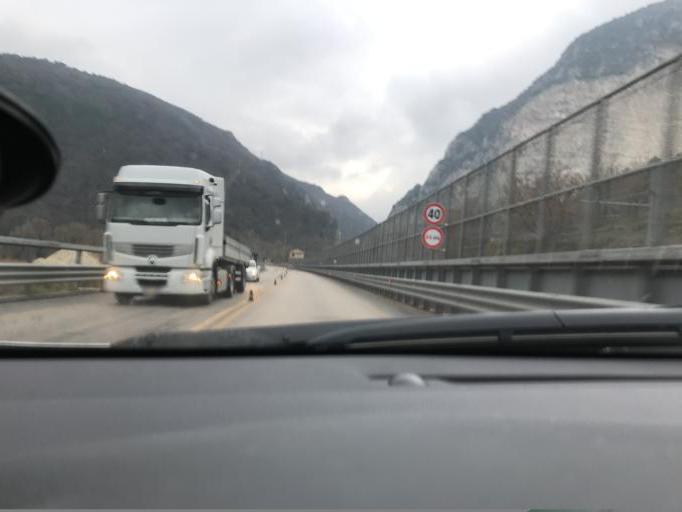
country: IT
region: The Marches
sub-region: Provincia di Ancona
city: Serra San Quirico
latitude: 43.4333
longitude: 13.0161
